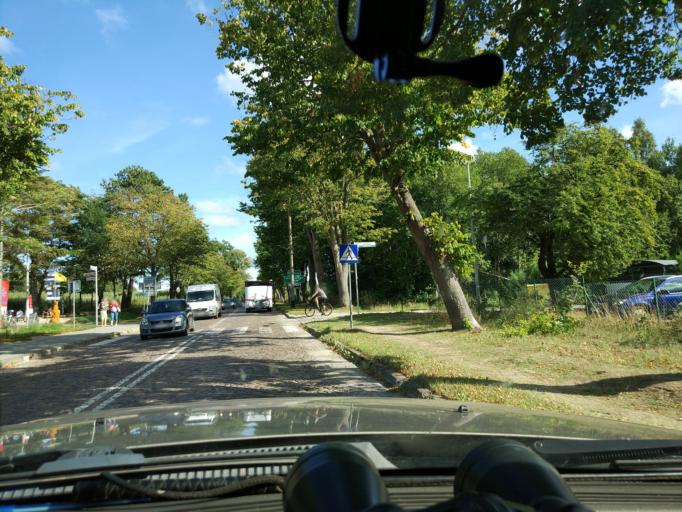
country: PL
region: Pomeranian Voivodeship
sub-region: Powiat pucki
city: Jastrzebia Gora
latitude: 54.8296
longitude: 18.3311
